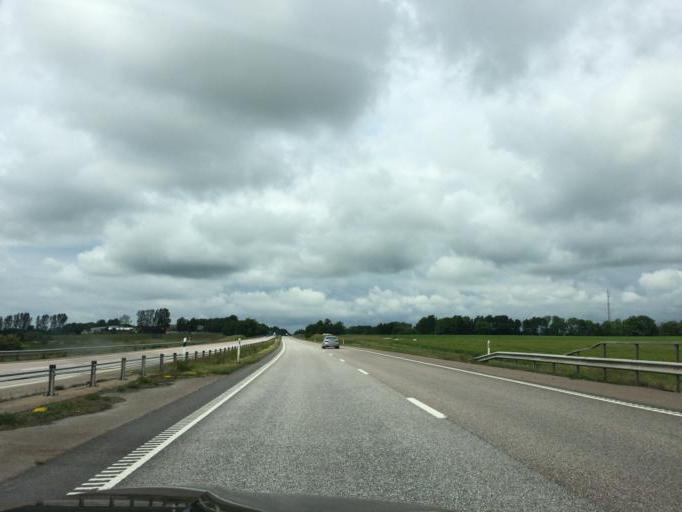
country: SE
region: Skane
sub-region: Angelholms Kommun
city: Strovelstorp
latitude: 56.1479
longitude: 12.8446
